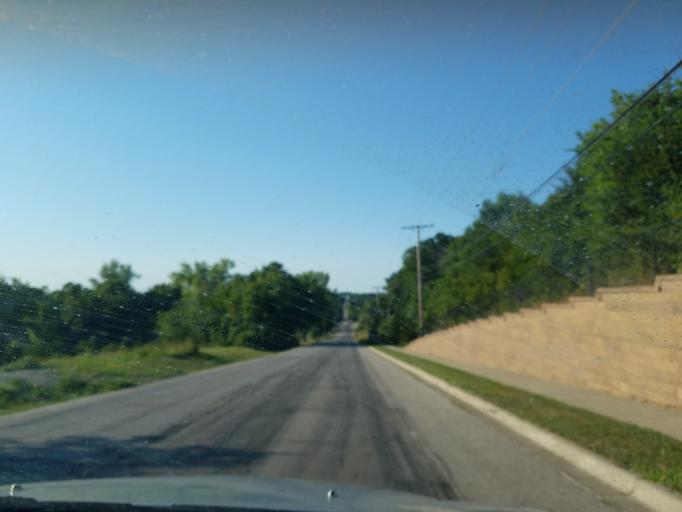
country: US
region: Missouri
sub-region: Clay County
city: Gladstone
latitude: 39.2197
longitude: -94.5347
